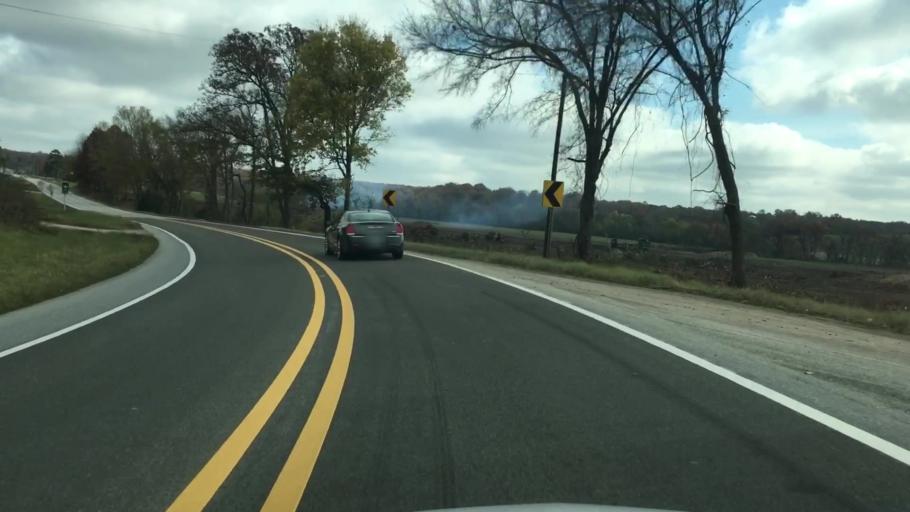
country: US
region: Arkansas
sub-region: Benton County
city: Gentry
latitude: 36.2560
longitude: -94.4489
